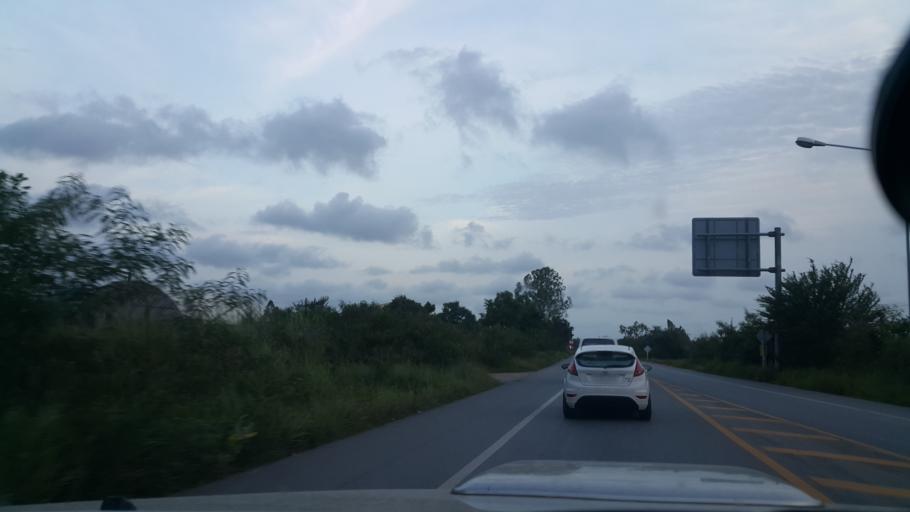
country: TH
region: Rayong
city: Ban Chang
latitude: 12.7250
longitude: 100.9833
